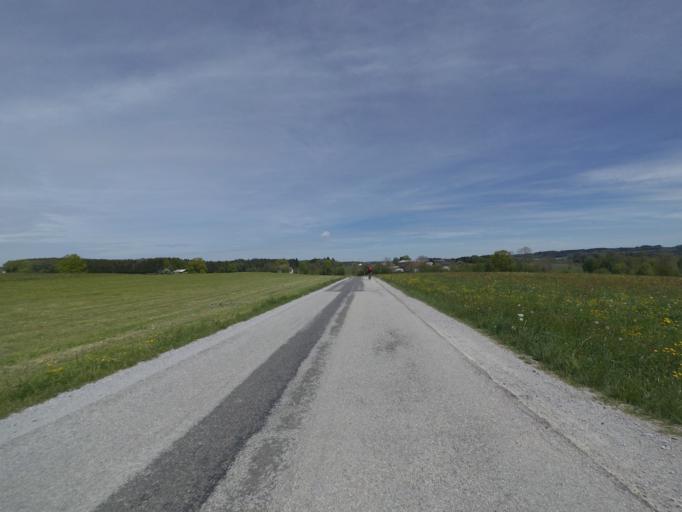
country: AT
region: Salzburg
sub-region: Politischer Bezirk Salzburg-Umgebung
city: Berndorf bei Salzburg
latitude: 47.9976
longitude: 13.0905
